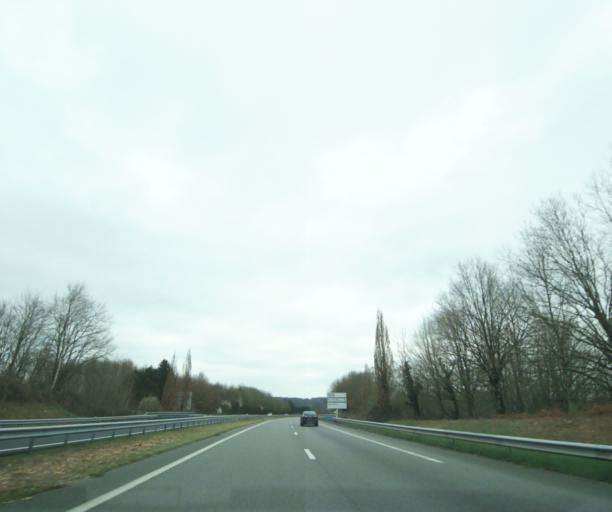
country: FR
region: Limousin
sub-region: Departement de la Correze
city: Uzerche
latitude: 45.3882
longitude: 1.5742
